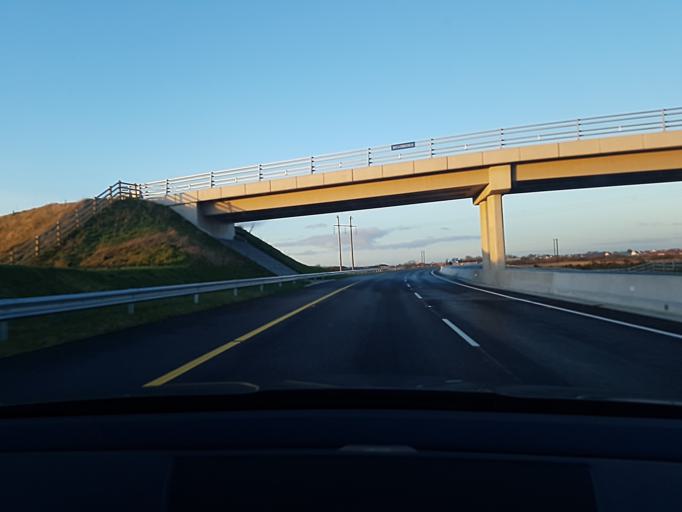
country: IE
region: Connaught
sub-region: County Galway
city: Tuam
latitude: 53.4989
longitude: -8.8786
